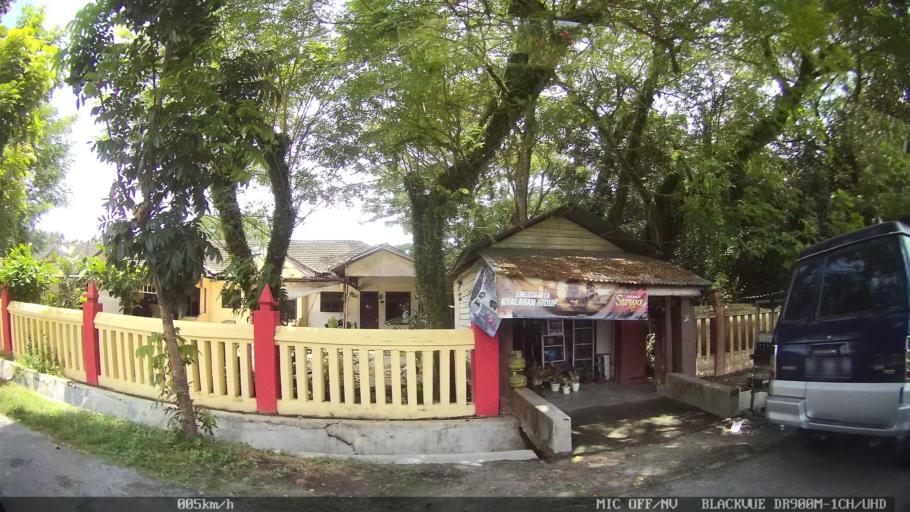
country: ID
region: North Sumatra
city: Percut
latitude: 3.5459
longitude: 98.8654
